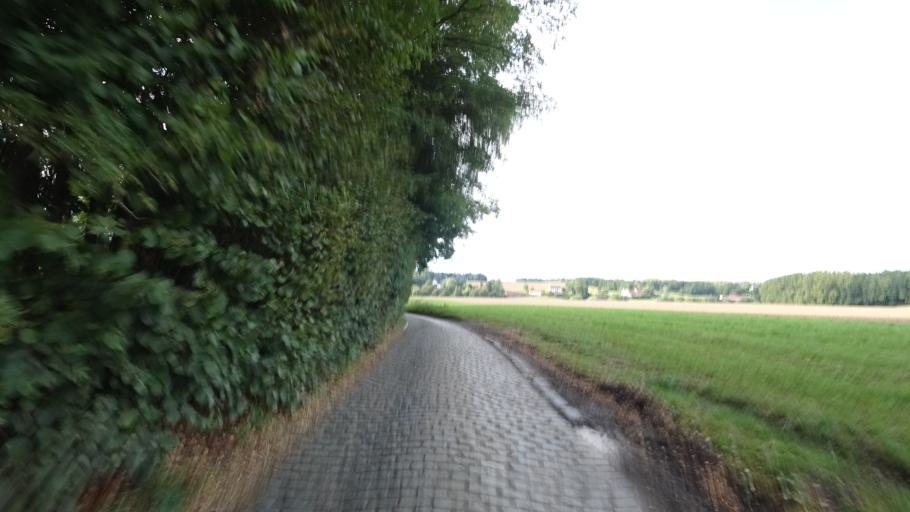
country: BE
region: Wallonia
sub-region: Province du Hainaut
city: Basse Lasne
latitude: 50.6777
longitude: 4.4463
